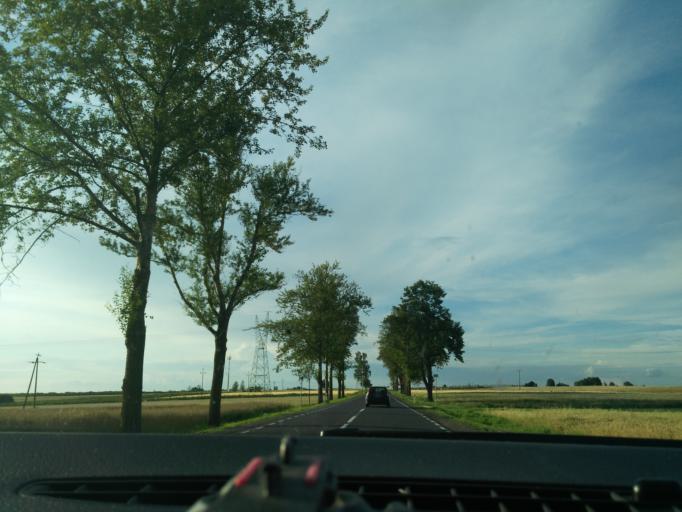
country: PL
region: Lublin Voivodeship
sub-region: Powiat krasnicki
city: Szastarka
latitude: 50.8121
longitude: 22.3194
